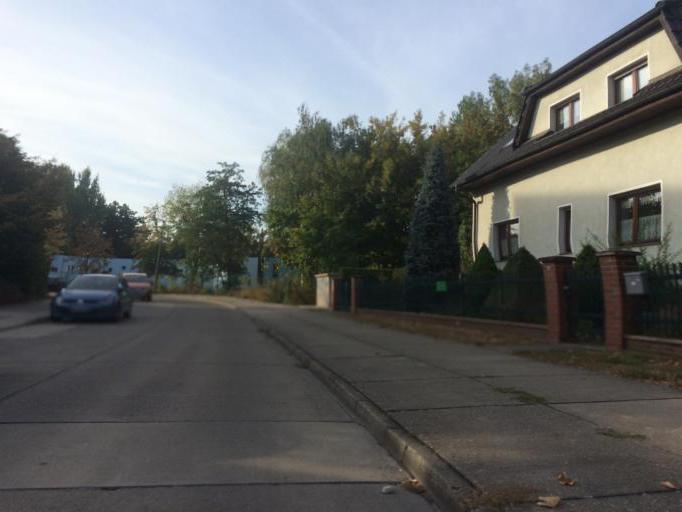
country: DE
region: Berlin
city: Alt-Hohenschoenhausen
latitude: 52.5499
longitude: 13.4951
